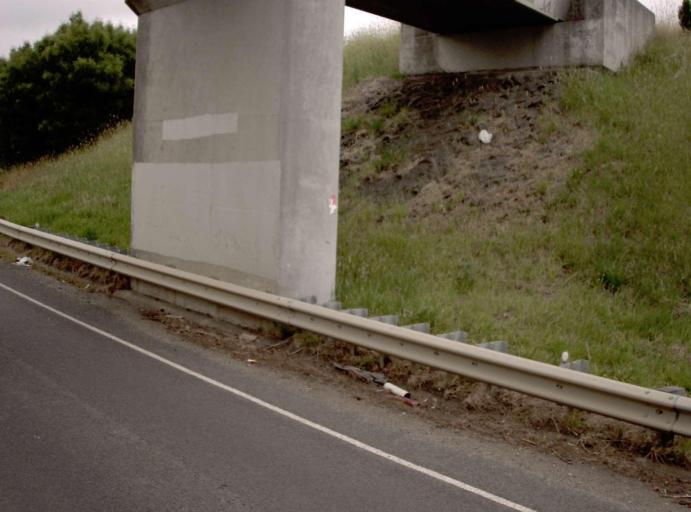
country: AU
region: Victoria
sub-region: Latrobe
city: Morwell
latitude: -38.2450
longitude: 146.4206
